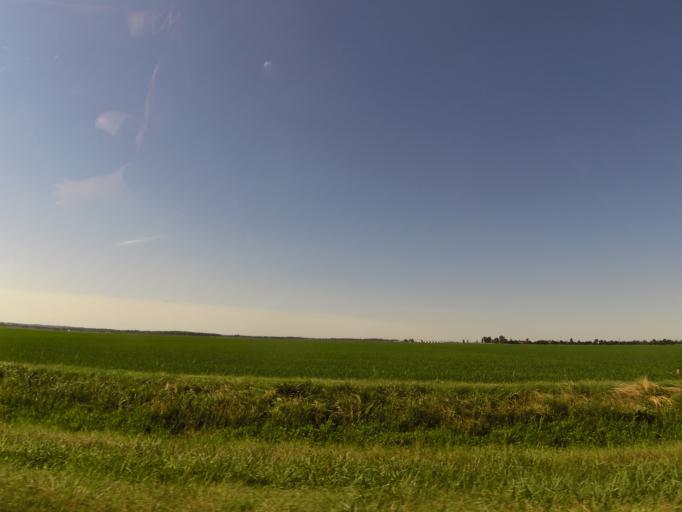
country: US
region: Arkansas
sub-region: Clay County
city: Corning
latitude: 36.4350
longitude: -90.4391
